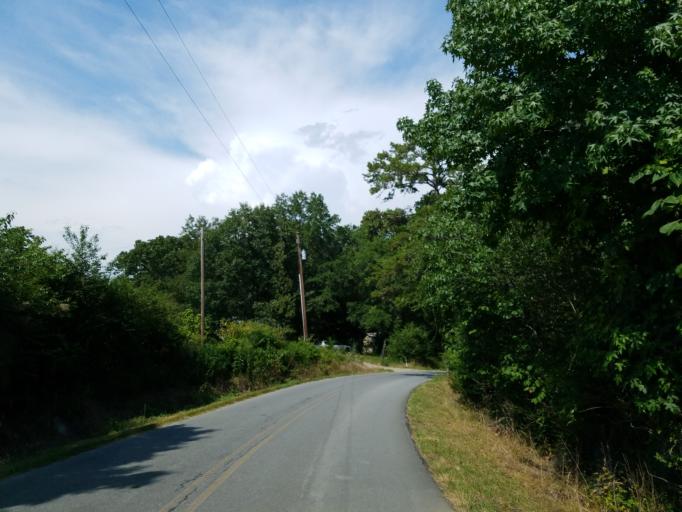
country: US
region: Georgia
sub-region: Bartow County
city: Rydal
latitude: 34.5353
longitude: -84.7276
